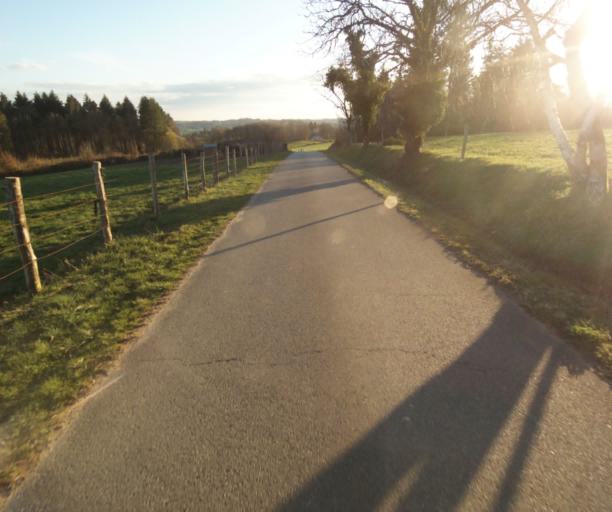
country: FR
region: Limousin
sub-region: Departement de la Correze
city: Uzerche
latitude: 45.3556
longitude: 1.5853
